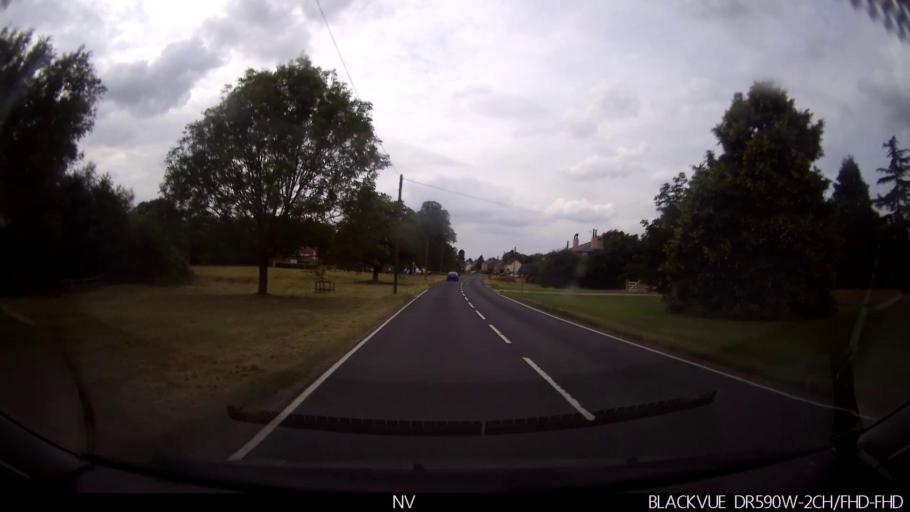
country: GB
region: England
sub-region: City of York
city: Holtby
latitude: 54.0495
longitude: -0.9603
